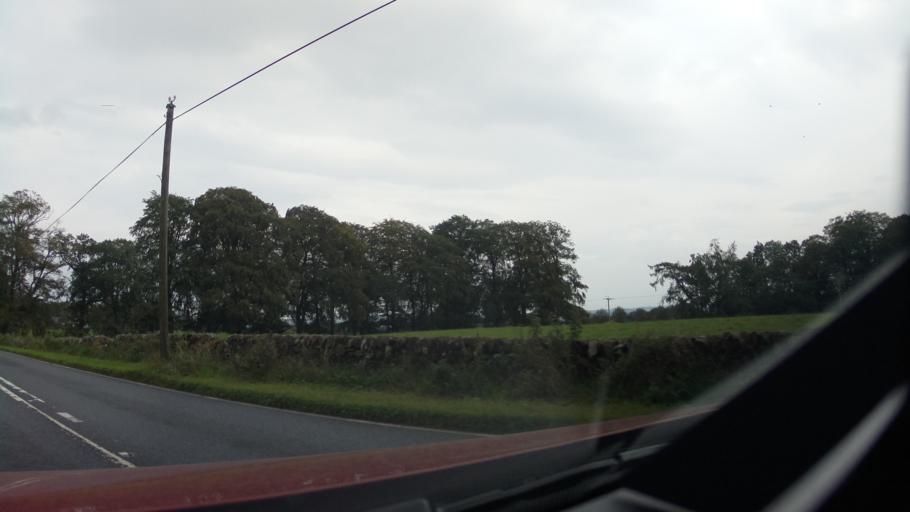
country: GB
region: Scotland
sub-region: Dumfries and Galloway
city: Lochmaben
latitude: 55.1986
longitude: -3.5012
